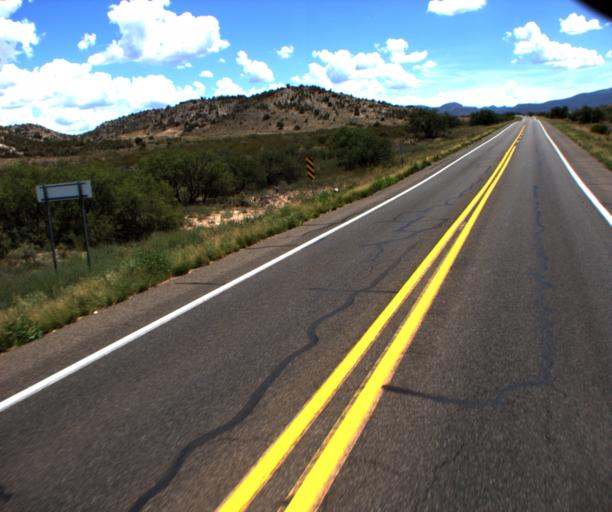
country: US
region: Arizona
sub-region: Yavapai County
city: Camp Verde
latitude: 34.5399
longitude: -111.8226
